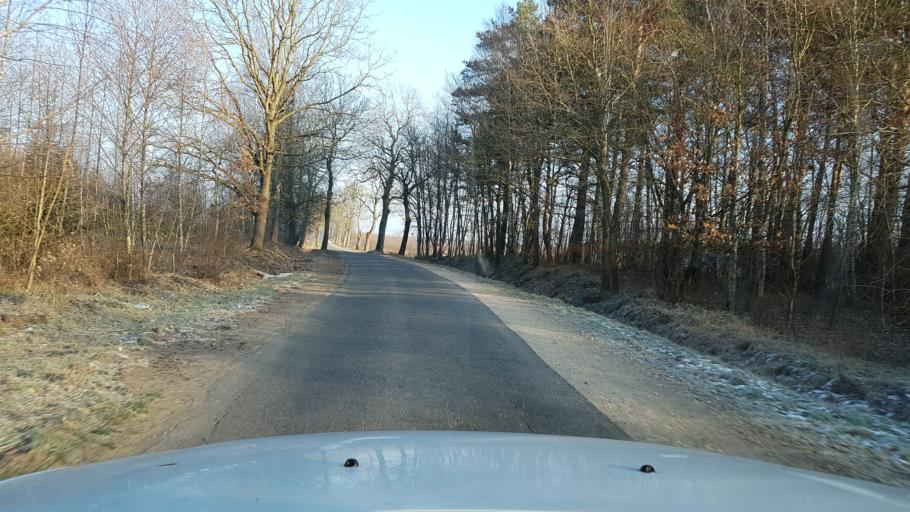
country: PL
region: West Pomeranian Voivodeship
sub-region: Powiat bialogardzki
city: Bialogard
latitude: 54.0599
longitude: 16.0804
